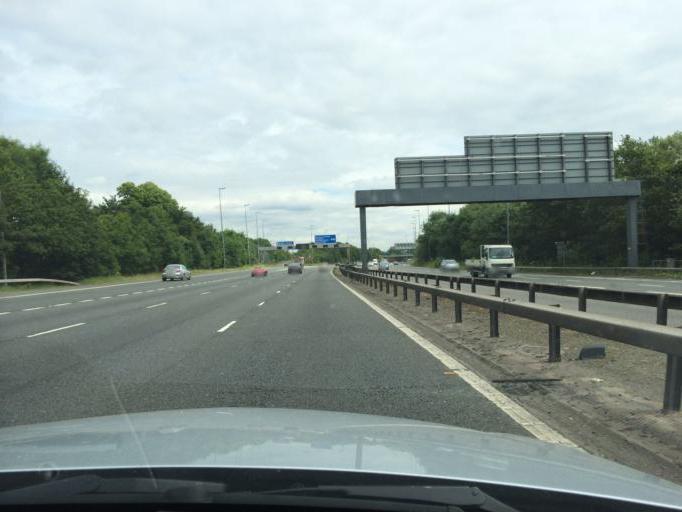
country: GB
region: England
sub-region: Manchester
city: Didsbury
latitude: 53.4007
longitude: -2.2158
